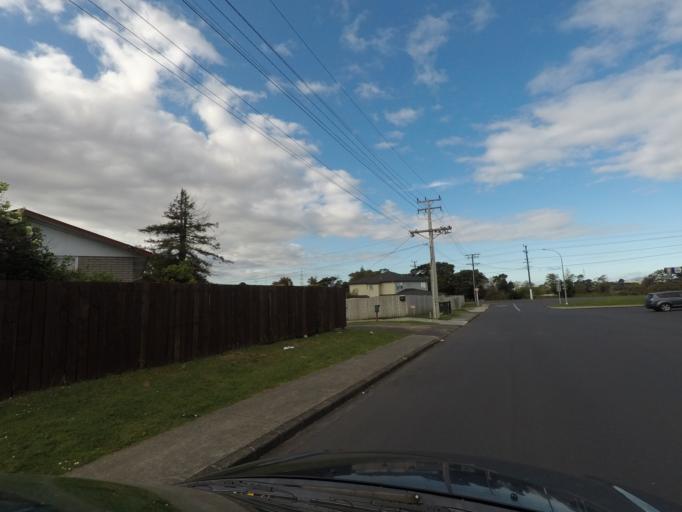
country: NZ
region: Auckland
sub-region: Auckland
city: Rosebank
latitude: -36.8840
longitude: 174.6567
